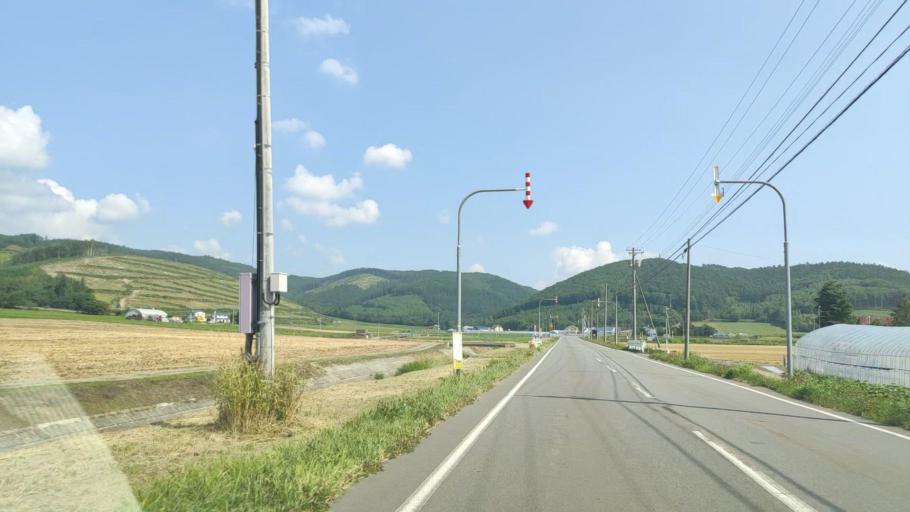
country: JP
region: Hokkaido
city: Shimo-furano
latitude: 43.4135
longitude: 142.3989
